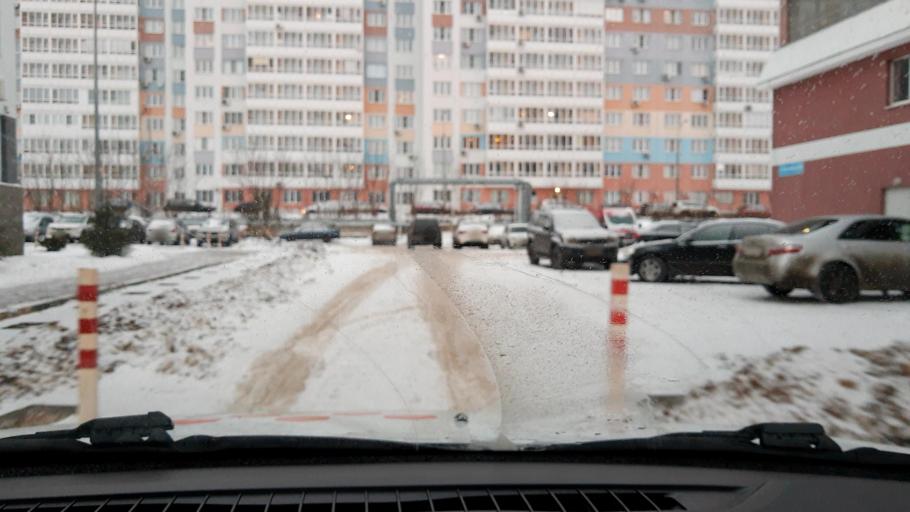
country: RU
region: Nizjnij Novgorod
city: Nizhniy Novgorod
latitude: 56.2836
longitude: 43.9872
